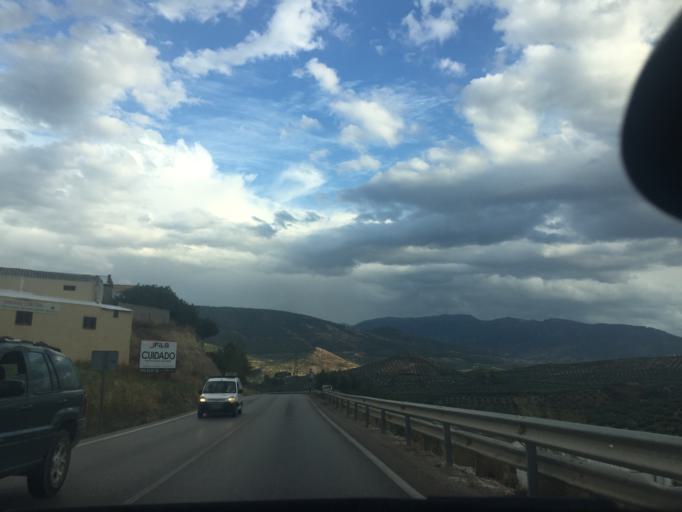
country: ES
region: Andalusia
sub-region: Provincia de Jaen
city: Jaen
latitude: 37.7657
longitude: -3.7735
